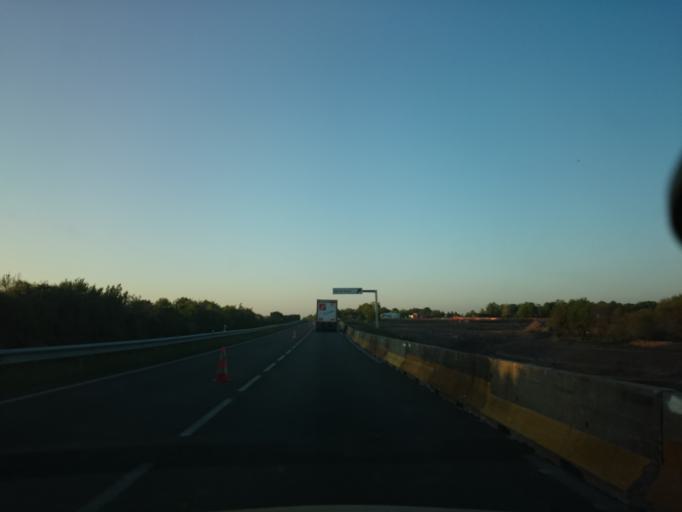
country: FR
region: Pays de la Loire
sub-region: Departement de la Loire-Atlantique
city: La Grigonnais
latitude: 47.5300
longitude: -1.6380
